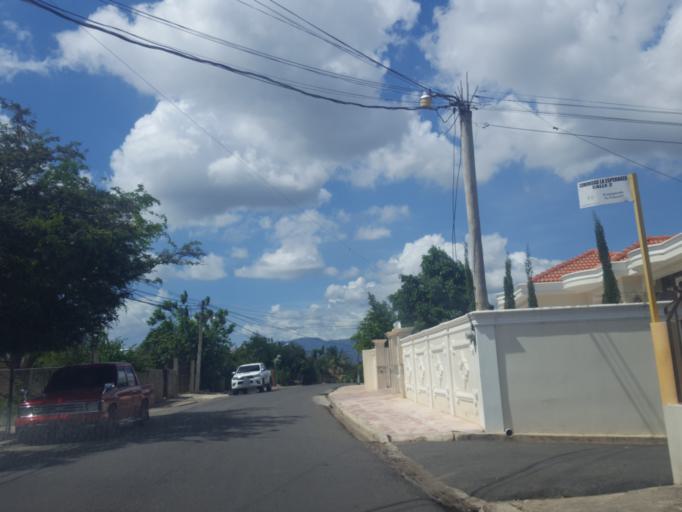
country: DO
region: Santiago
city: Licey al Medio
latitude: 19.3920
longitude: -70.6484
